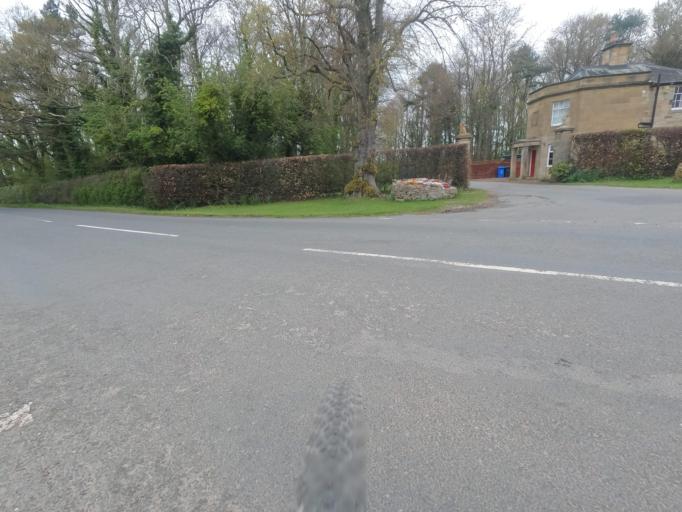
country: GB
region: England
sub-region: Northumberland
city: Ponteland
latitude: 55.0837
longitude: -1.7642
